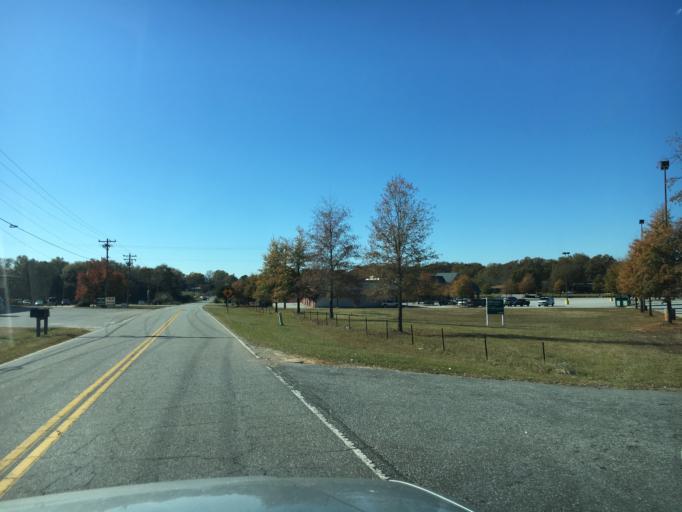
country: US
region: South Carolina
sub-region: Anderson County
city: Centerville
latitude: 34.5095
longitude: -82.7581
